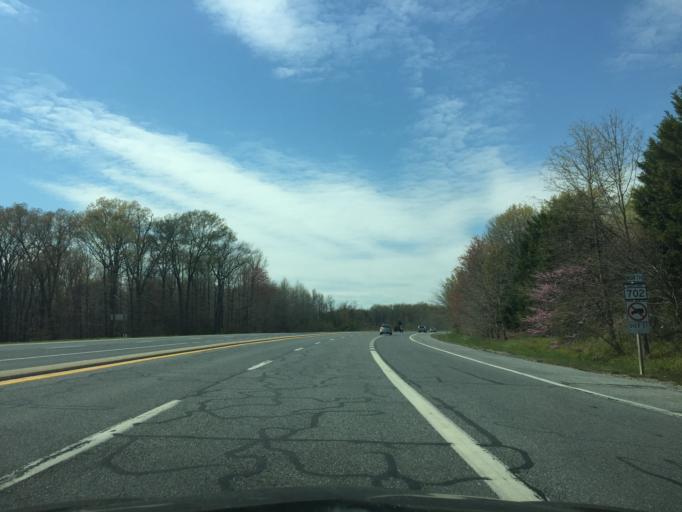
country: US
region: Maryland
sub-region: Baltimore County
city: Middle River
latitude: 39.2931
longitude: -76.4321
